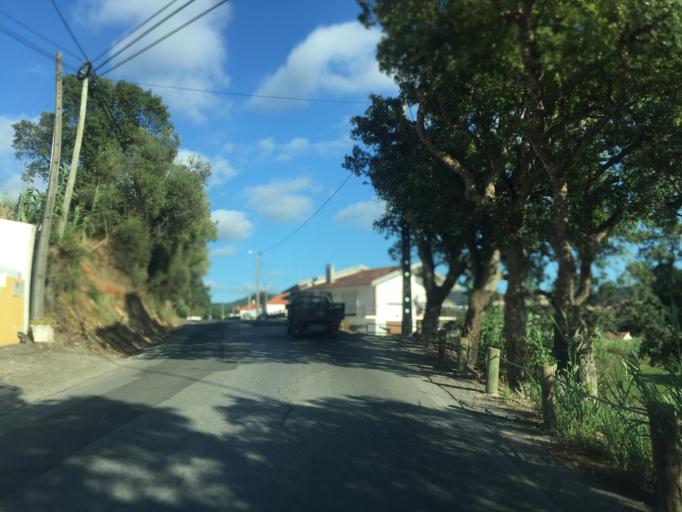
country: PT
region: Lisbon
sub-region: Torres Vedras
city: A dos Cunhados
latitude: 39.1477
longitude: -9.2872
